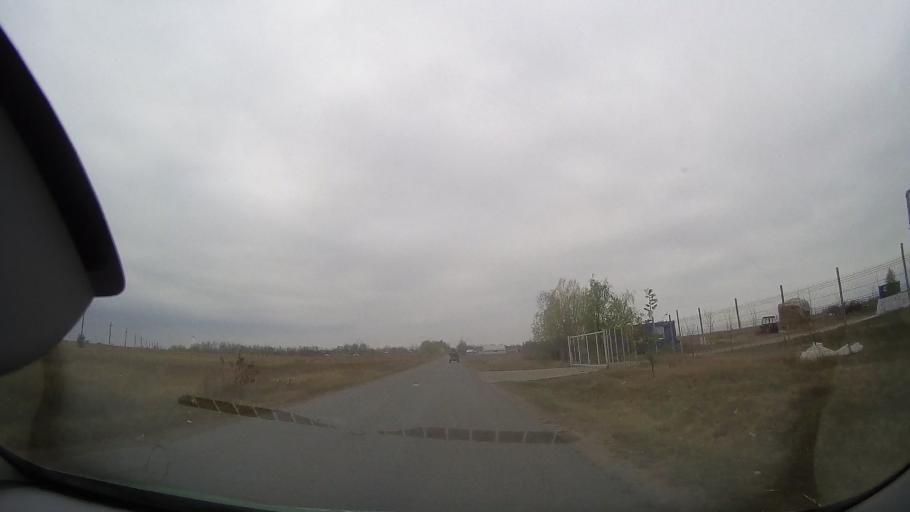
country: RO
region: Buzau
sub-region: Comuna Luciu
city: Luciu
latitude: 44.9675
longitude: 27.0980
